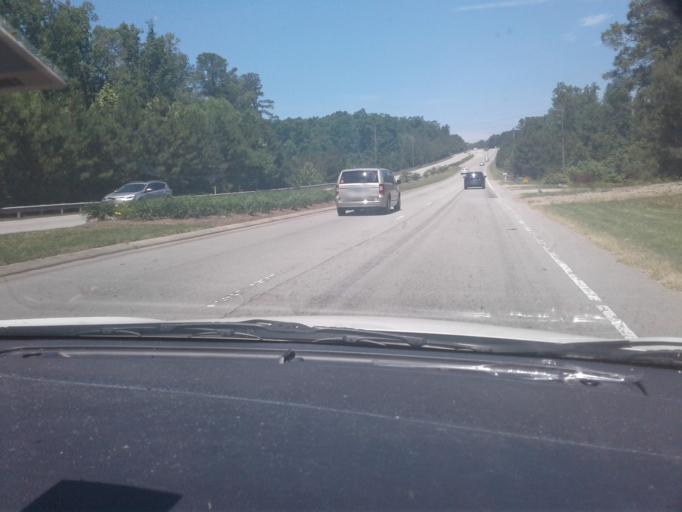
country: US
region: North Carolina
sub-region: Wake County
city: Holly Springs
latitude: 35.6200
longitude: -78.8162
